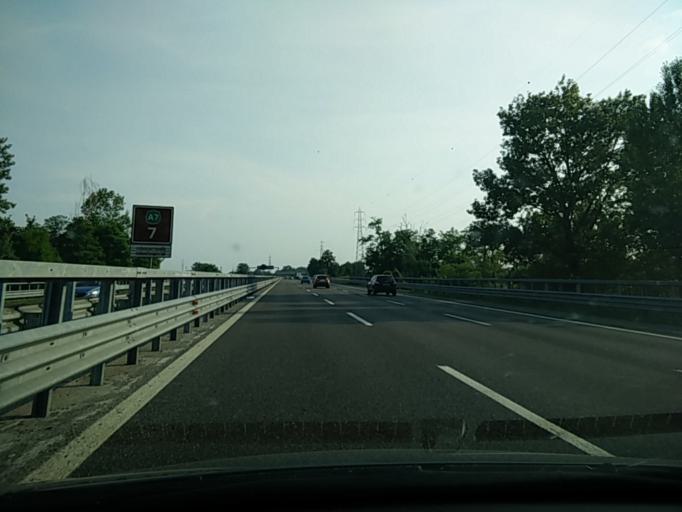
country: IT
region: Lombardy
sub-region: Citta metropolitana di Milano
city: Rozzano
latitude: 45.3818
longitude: 9.1342
